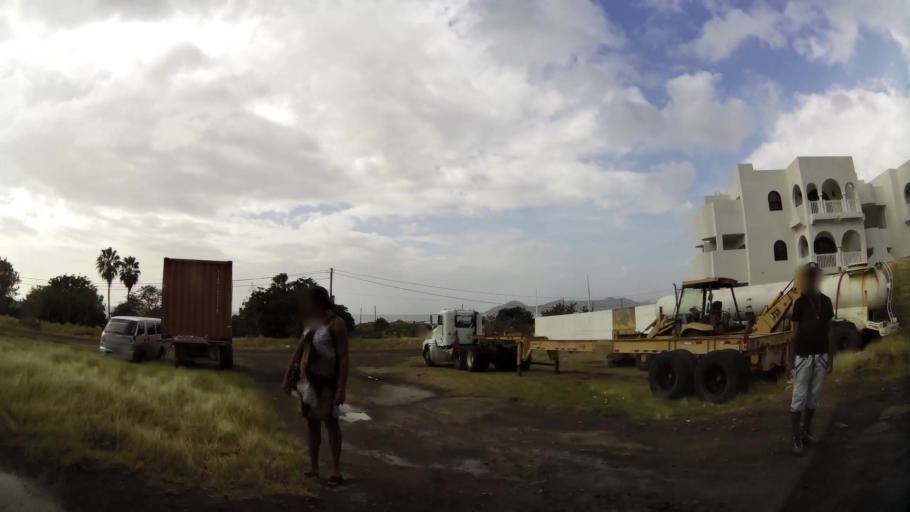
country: KN
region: Saint Thomas Lowland
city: Cotton Ground
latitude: 17.1864
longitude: -62.6178
